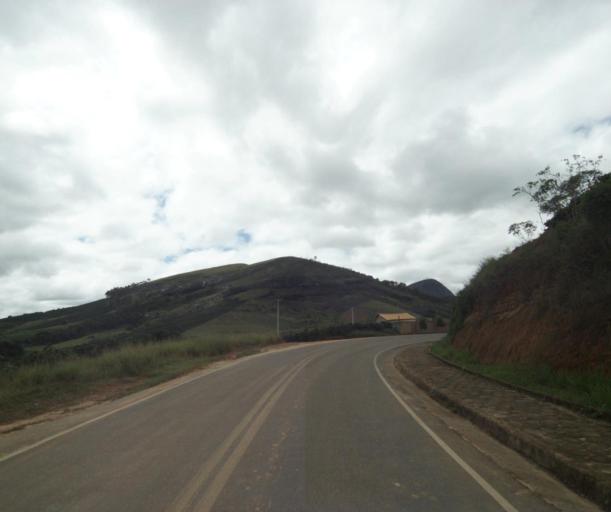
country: BR
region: Espirito Santo
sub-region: Irupi
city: Irupi
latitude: -20.3509
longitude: -41.6272
